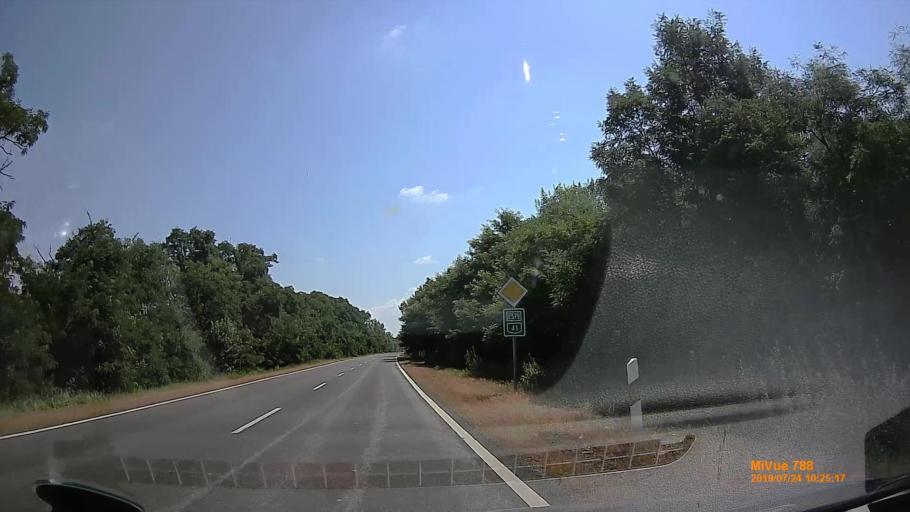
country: HU
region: Szabolcs-Szatmar-Bereg
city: Vasarosnameny
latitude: 48.1516
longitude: 22.4048
